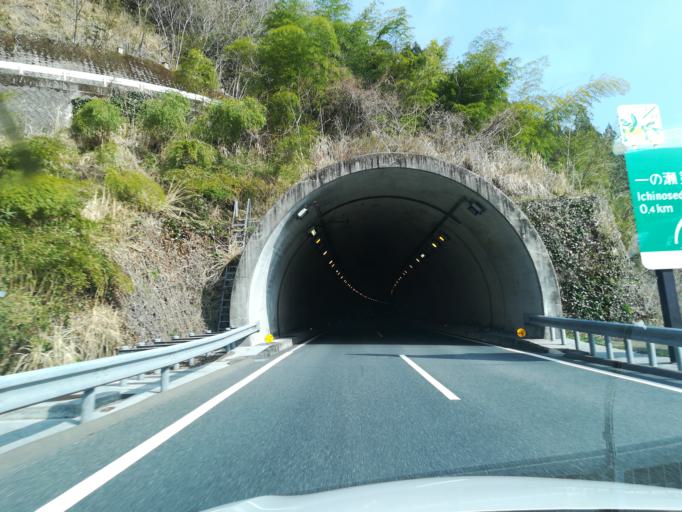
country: JP
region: Ehime
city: Kawanoecho
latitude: 33.7992
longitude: 133.6614
